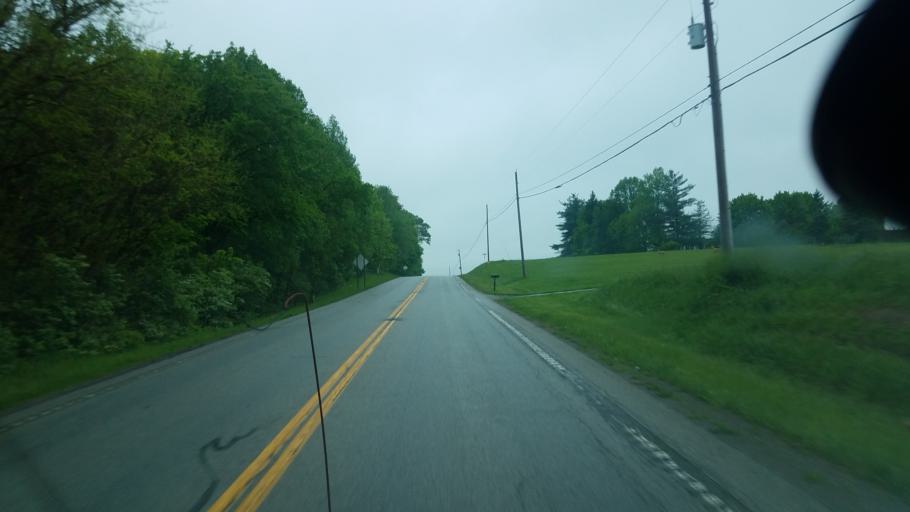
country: US
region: Ohio
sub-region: Highland County
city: Hillsboro
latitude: 39.2622
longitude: -83.5993
